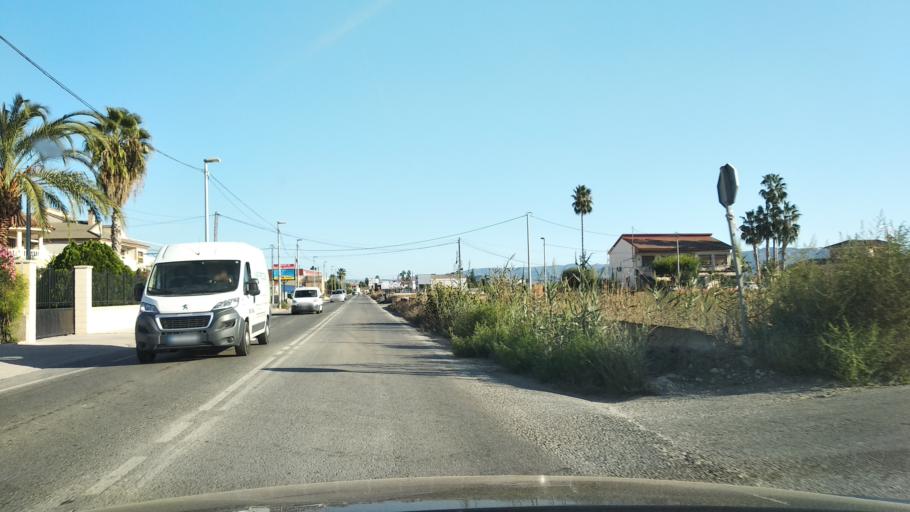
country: ES
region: Murcia
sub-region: Murcia
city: Santomera
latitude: 38.0447
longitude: -1.0528
